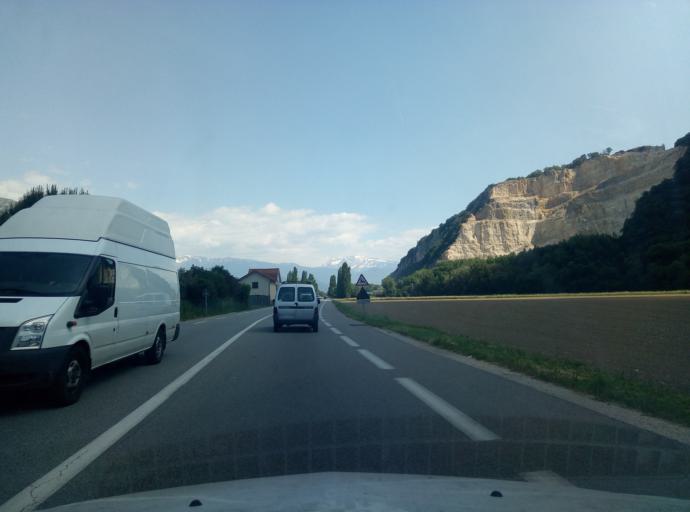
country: FR
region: Rhone-Alpes
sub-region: Departement de l'Isere
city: Noyarey
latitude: 45.2362
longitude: 5.6384
